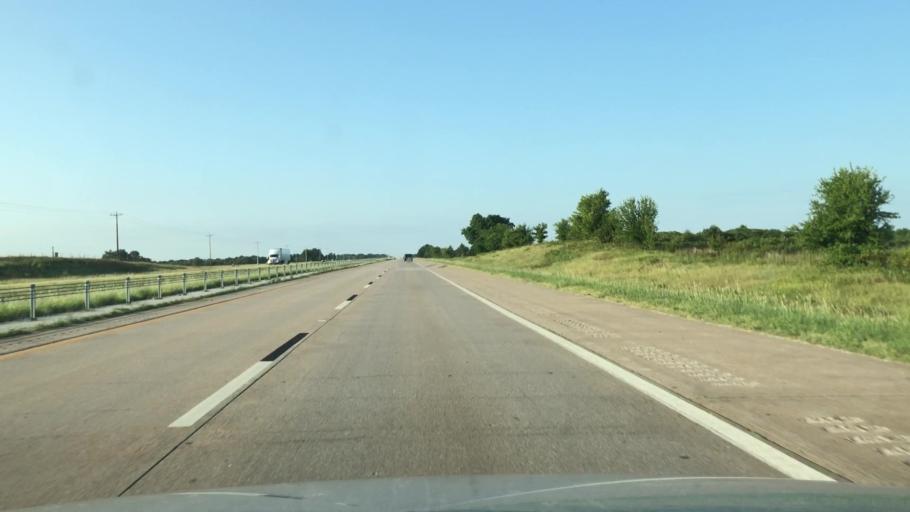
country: US
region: Oklahoma
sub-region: Osage County
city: Skiatook
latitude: 36.4511
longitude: -95.9207
